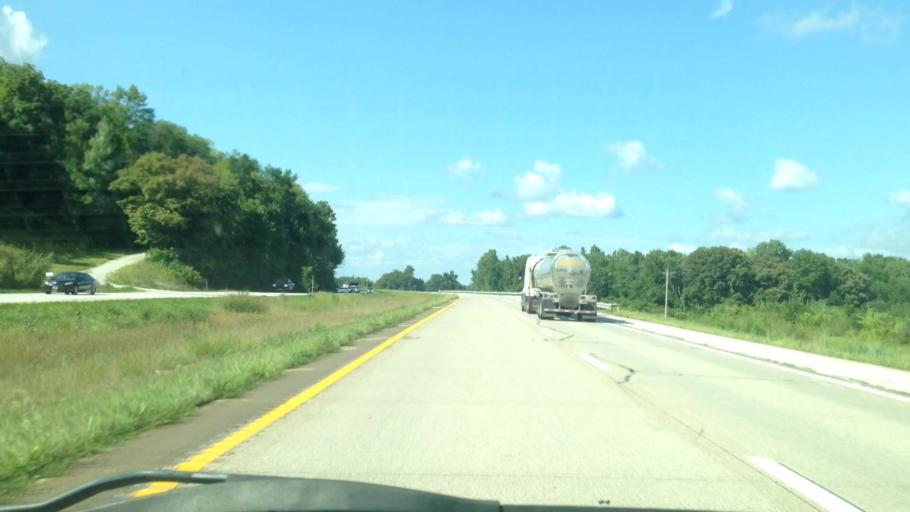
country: US
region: Missouri
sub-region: Lewis County
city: Canton
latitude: 40.1869
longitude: -91.5212
